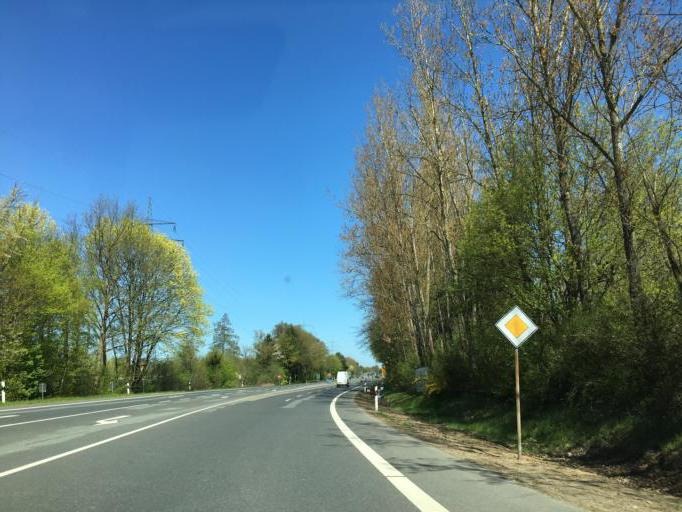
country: DE
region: Hesse
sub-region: Regierungsbezirk Darmstadt
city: Neu Isenburg
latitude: 50.0571
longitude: 8.7251
